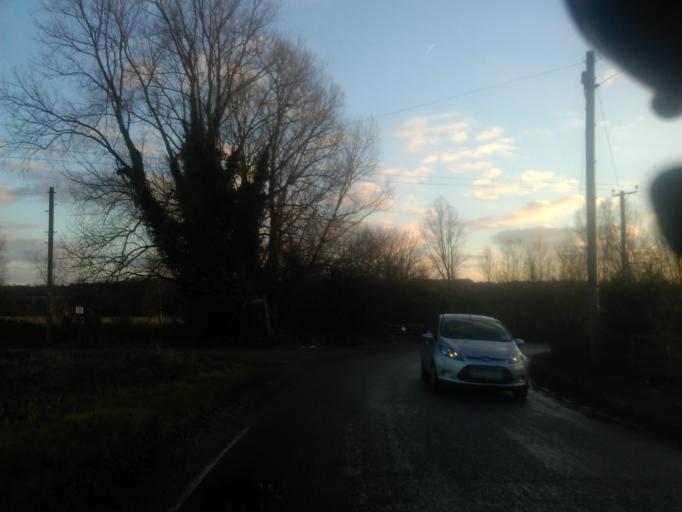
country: GB
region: England
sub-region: Essex
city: Hatfield Peverel
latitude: 51.7530
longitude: 0.5741
